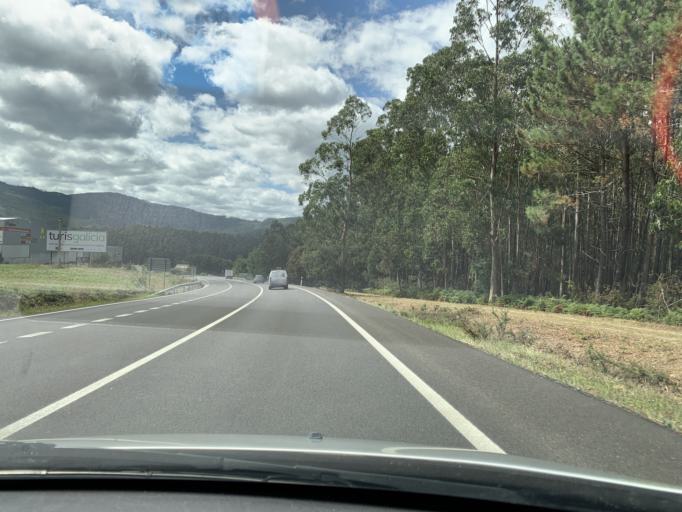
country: ES
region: Galicia
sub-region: Provincia de Lugo
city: Barreiros
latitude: 43.5405
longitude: -7.2600
